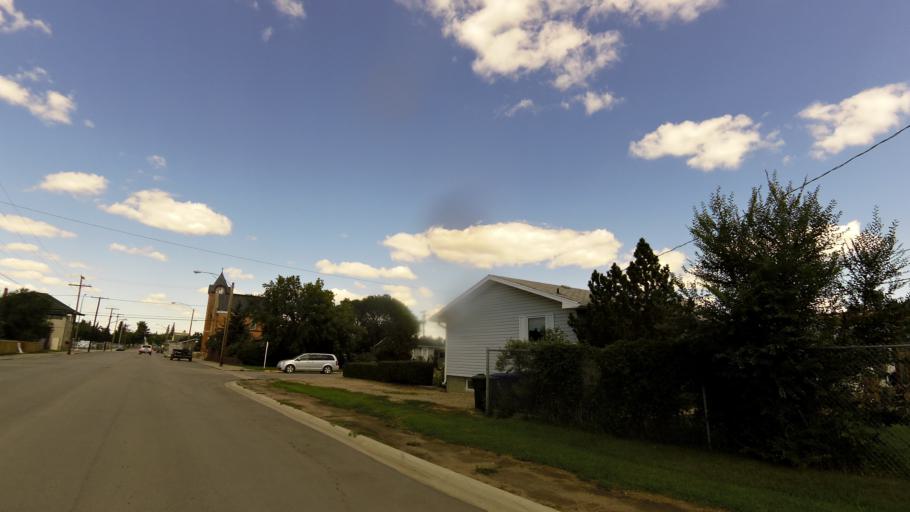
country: CA
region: Saskatchewan
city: North Battleford
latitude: 52.7350
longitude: -108.3085
